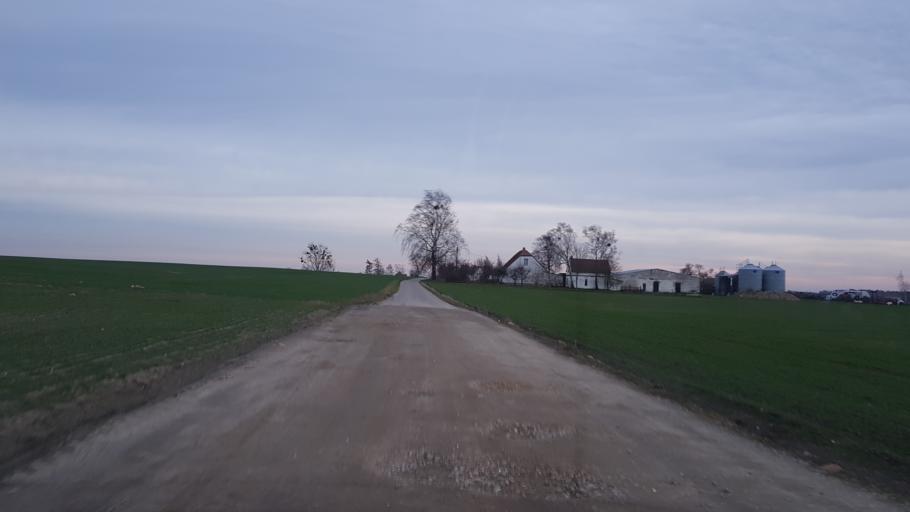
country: PL
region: West Pomeranian Voivodeship
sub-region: Powiat choszczenski
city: Pelczyce
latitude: 53.0333
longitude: 15.2663
